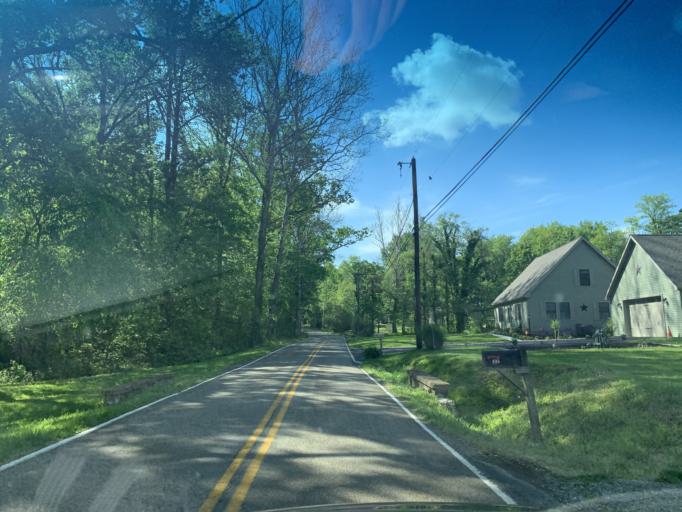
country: US
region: Maryland
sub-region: Cecil County
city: Rising Sun
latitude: 39.6951
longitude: -76.1545
